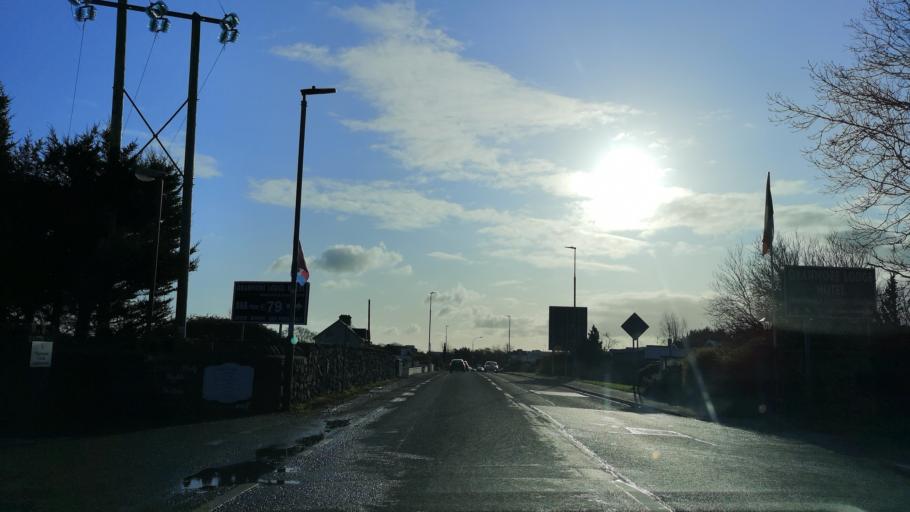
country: IE
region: Connaught
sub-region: County Galway
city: Oranmore
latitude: 53.2749
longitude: -8.9276
